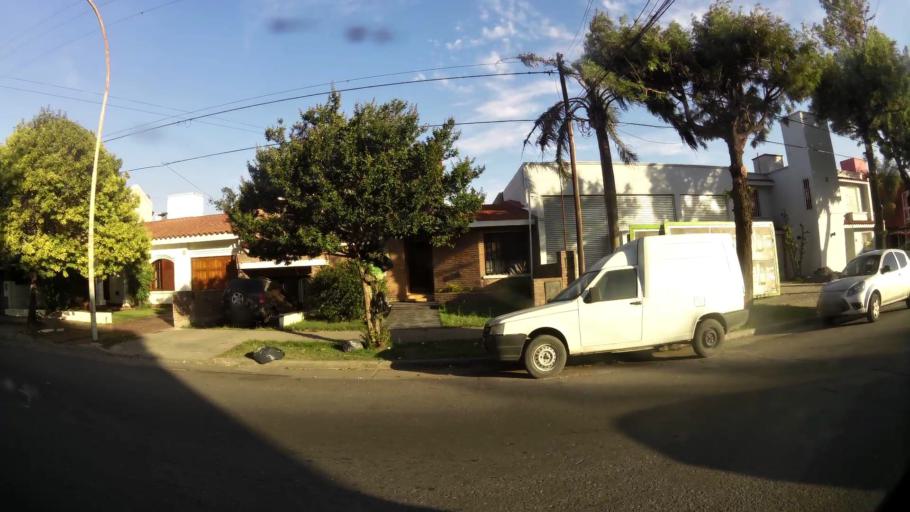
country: AR
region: Cordoba
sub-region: Departamento de Capital
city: Cordoba
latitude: -31.3802
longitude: -64.2447
